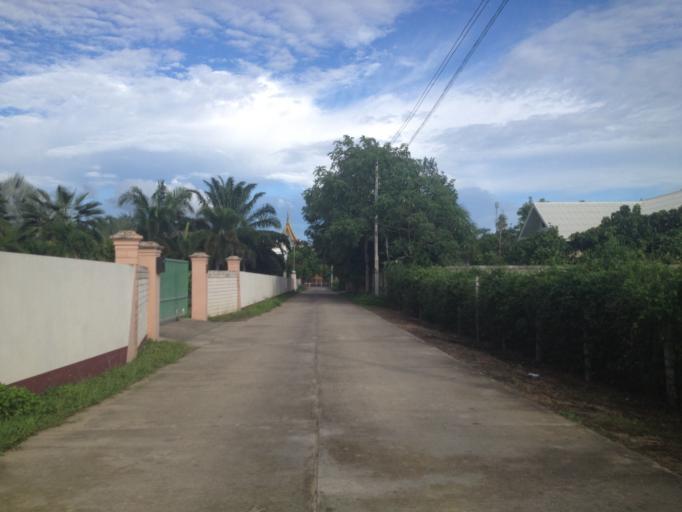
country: TH
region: Chiang Mai
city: Hang Dong
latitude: 18.6812
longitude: 98.8946
